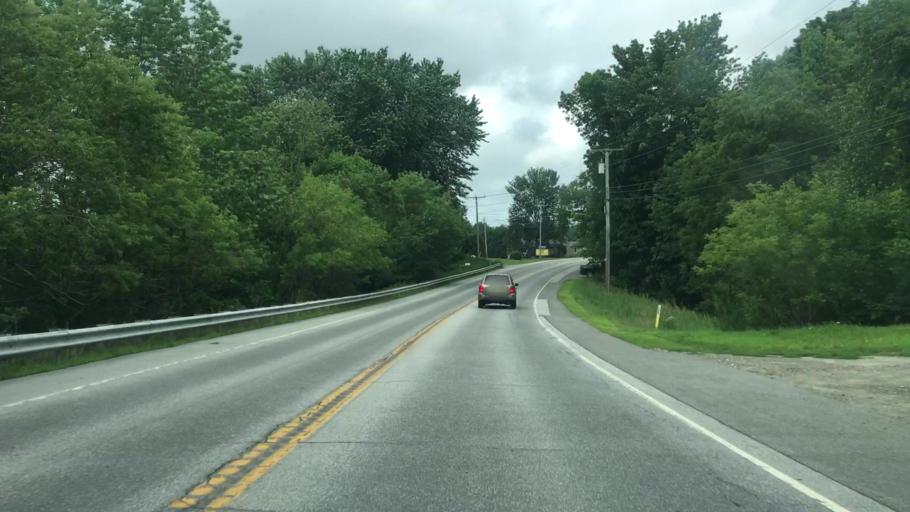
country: US
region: Maine
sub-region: Kennebec County
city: Hallowell
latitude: 44.2812
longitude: -69.7764
